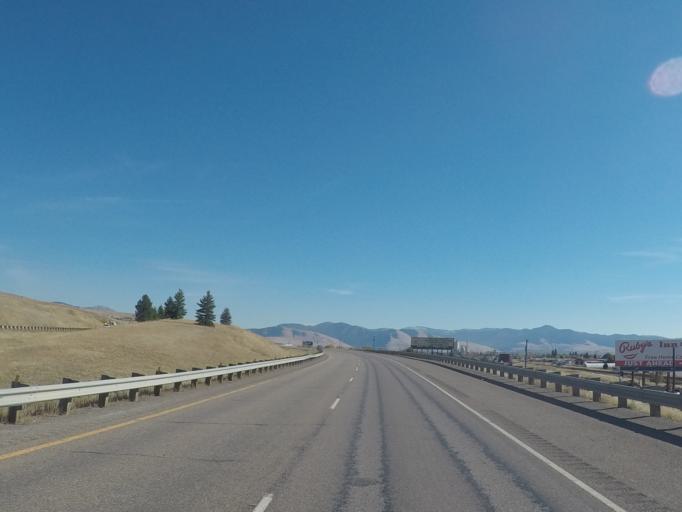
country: US
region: Montana
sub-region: Missoula County
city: Orchard Homes
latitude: 46.9404
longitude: -114.1123
